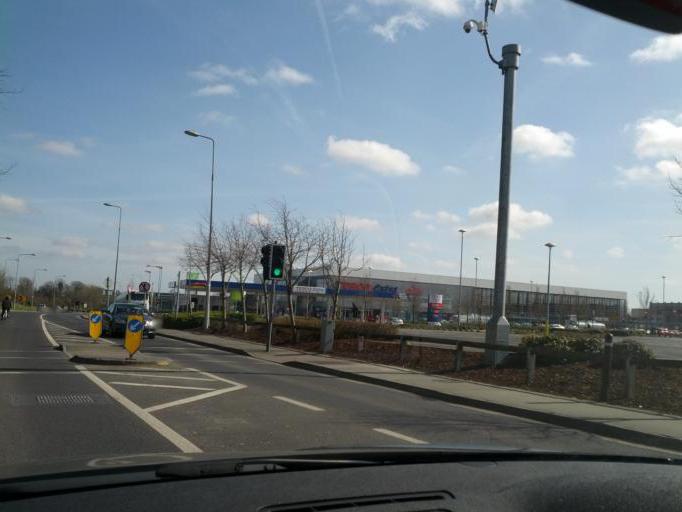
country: IE
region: Leinster
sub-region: Kildare
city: Maynooth
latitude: 53.3820
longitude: -6.5850
